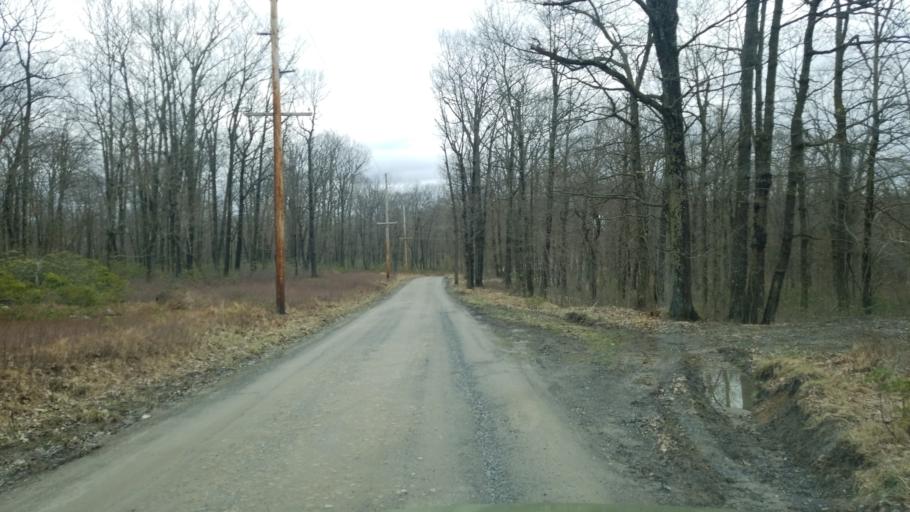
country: US
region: Pennsylvania
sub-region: Clearfield County
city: Shiloh
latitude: 41.1744
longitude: -78.3069
